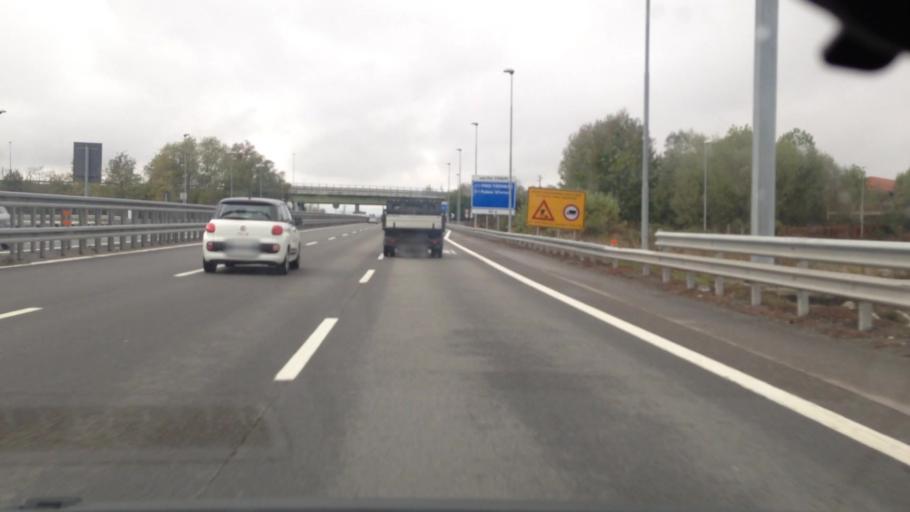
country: IT
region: Piedmont
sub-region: Provincia di Asti
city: Villanova d'Asti
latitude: 44.9536
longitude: 7.9194
